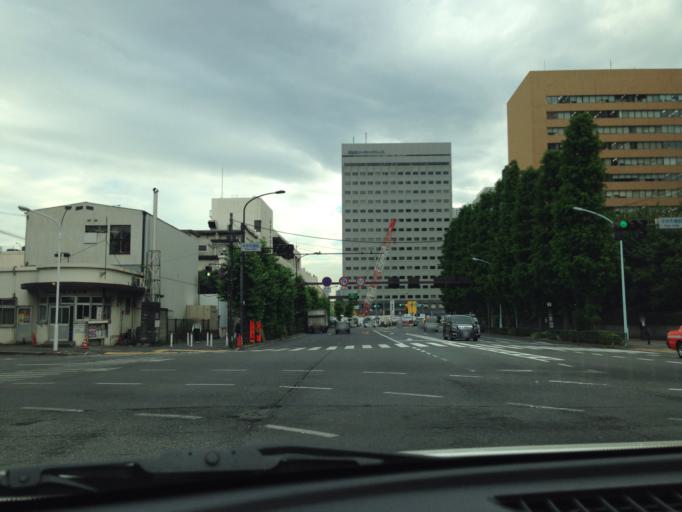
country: JP
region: Tokyo
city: Tokyo
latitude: 35.6642
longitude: 139.7680
